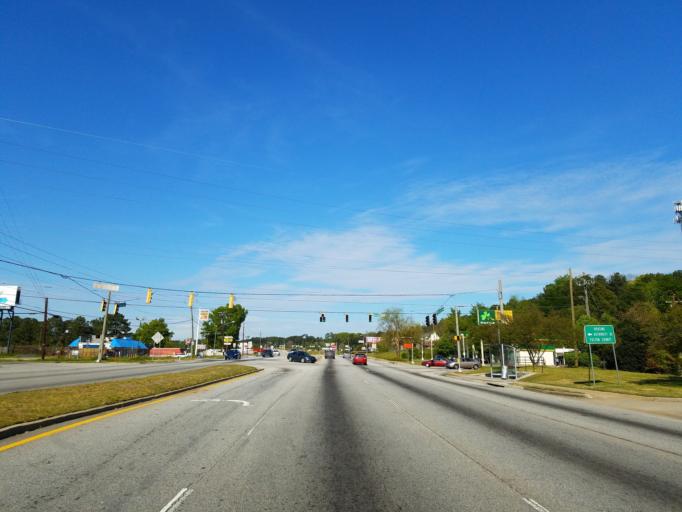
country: US
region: Georgia
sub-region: Cobb County
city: Mableton
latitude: 33.7676
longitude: -84.5248
